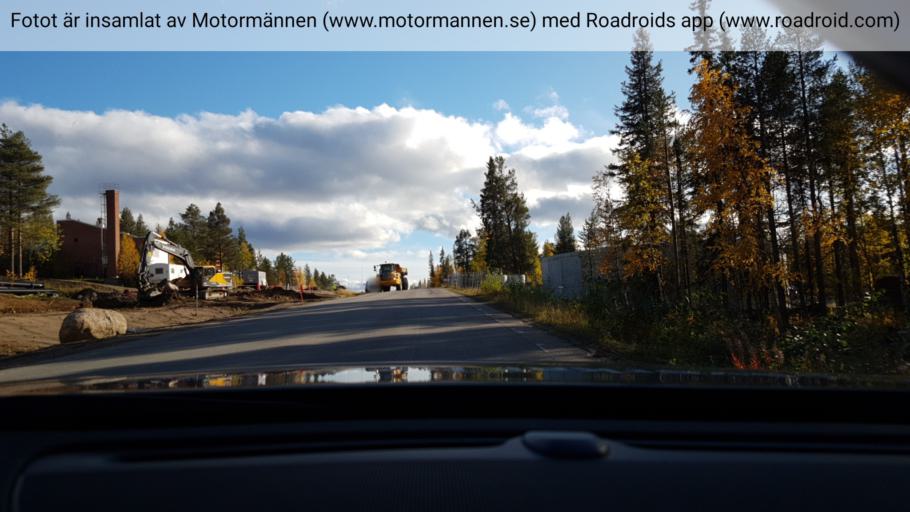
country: SE
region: Norrbotten
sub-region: Gallivare Kommun
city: Gaellivare
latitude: 67.1196
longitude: 20.6558
